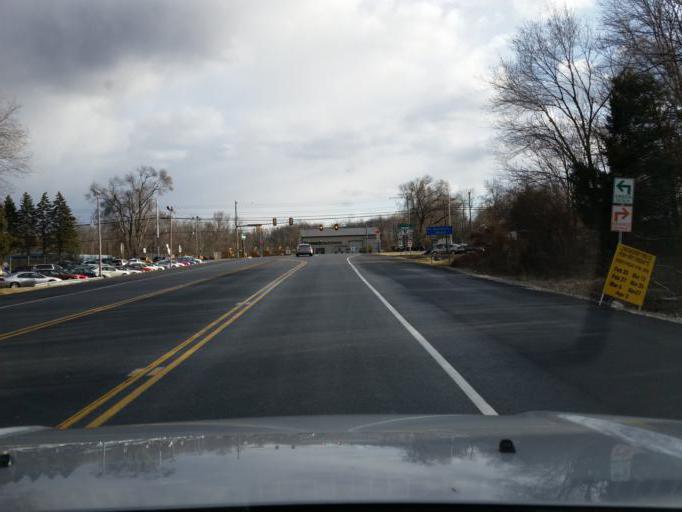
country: US
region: Pennsylvania
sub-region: Dauphin County
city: Middletown
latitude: 40.1924
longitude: -76.6862
